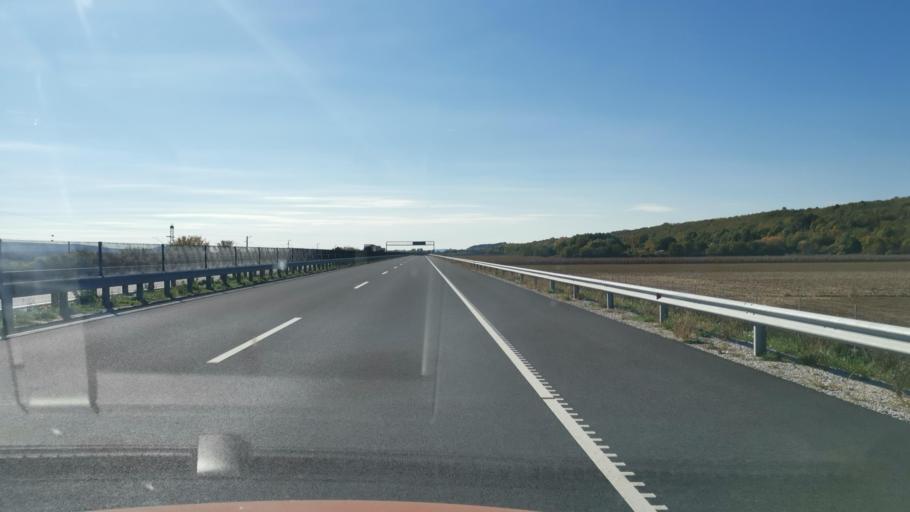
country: HU
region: Borsod-Abauj-Zemplen
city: Gonc
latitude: 48.4418
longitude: 21.1900
